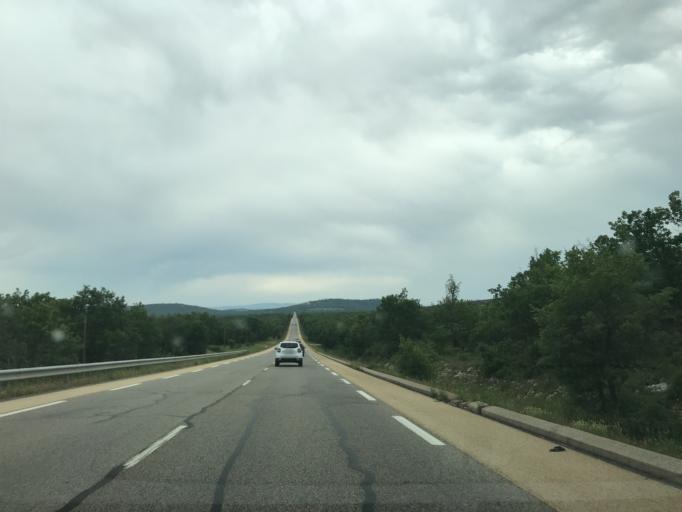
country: FR
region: Provence-Alpes-Cote d'Azur
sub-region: Departement du Var
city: Rians
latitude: 43.5462
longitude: 5.8029
